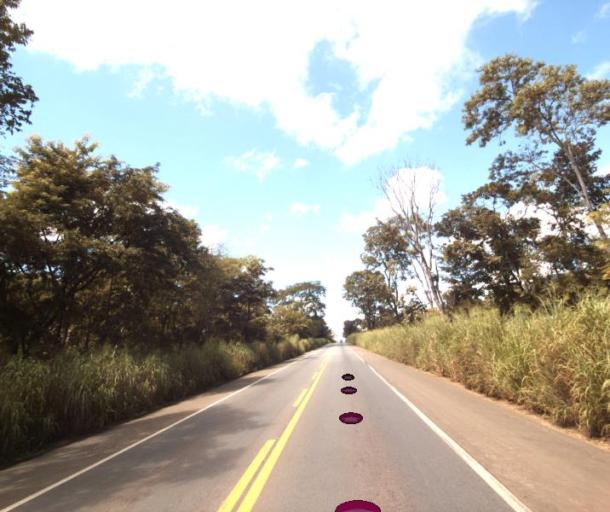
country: BR
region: Goias
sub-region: Jaragua
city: Jaragua
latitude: -15.7921
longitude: -49.3019
